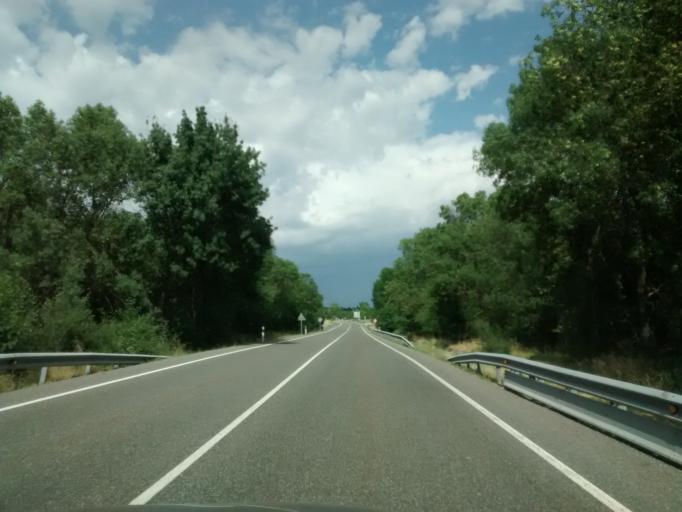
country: ES
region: Castille and Leon
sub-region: Provincia de Segovia
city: Matabuena
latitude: 41.0949
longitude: -3.7635
